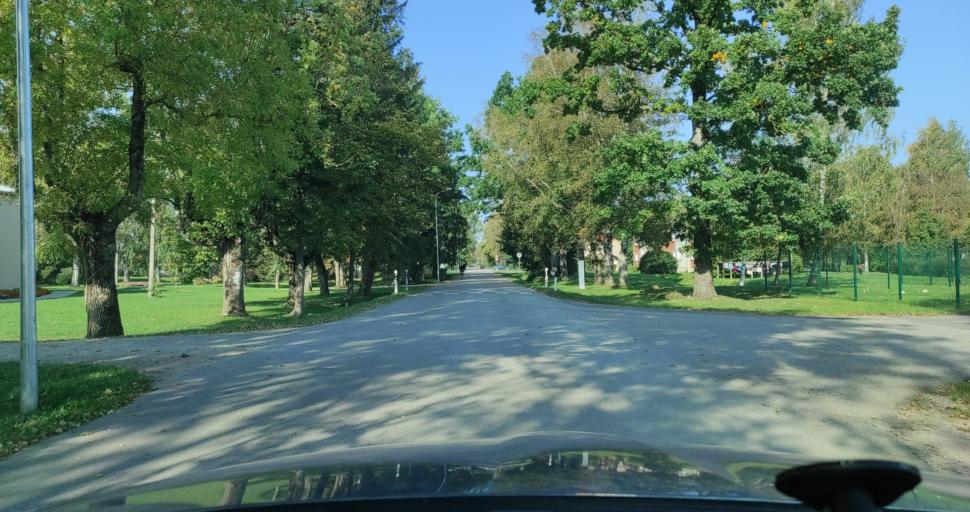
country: LV
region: Ventspils Rajons
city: Piltene
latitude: 57.2254
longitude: 21.6082
